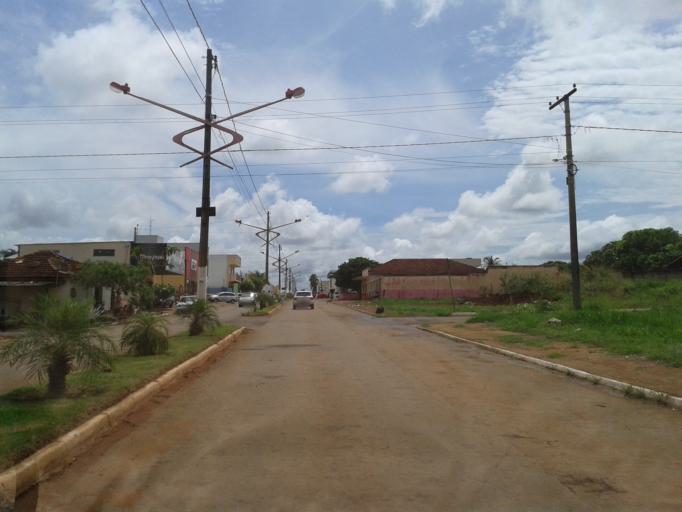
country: BR
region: Goias
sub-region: Buriti Alegre
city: Buriti Alegre
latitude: -18.1309
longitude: -49.0384
